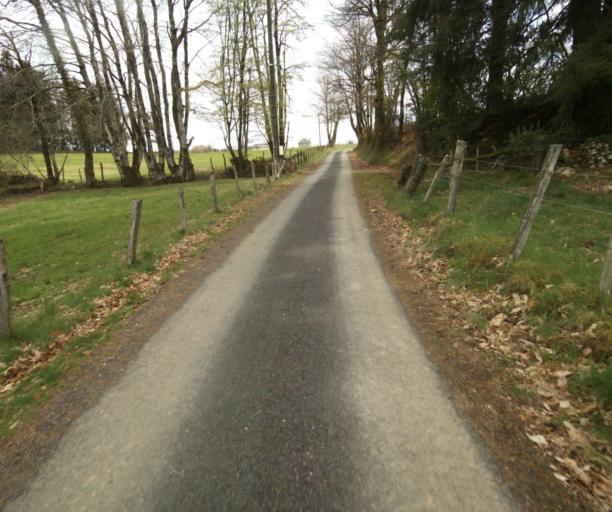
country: FR
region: Limousin
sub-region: Departement de la Correze
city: Laguenne
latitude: 45.2058
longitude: 1.8776
